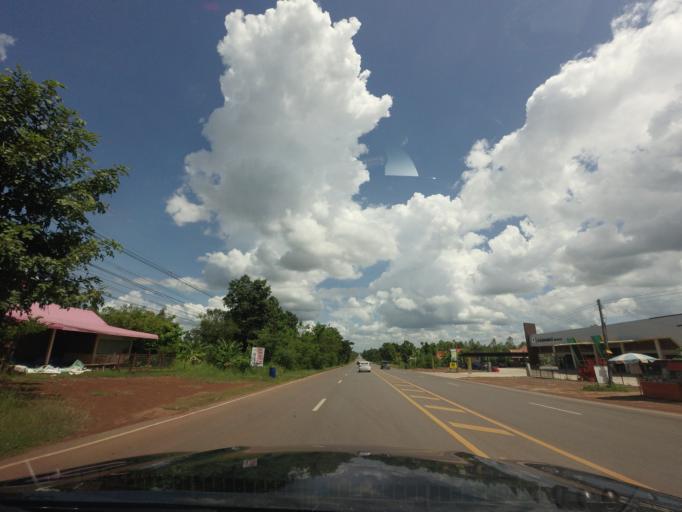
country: TH
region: Changwat Udon Thani
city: Ban Dung
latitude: 17.6838
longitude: 103.2146
